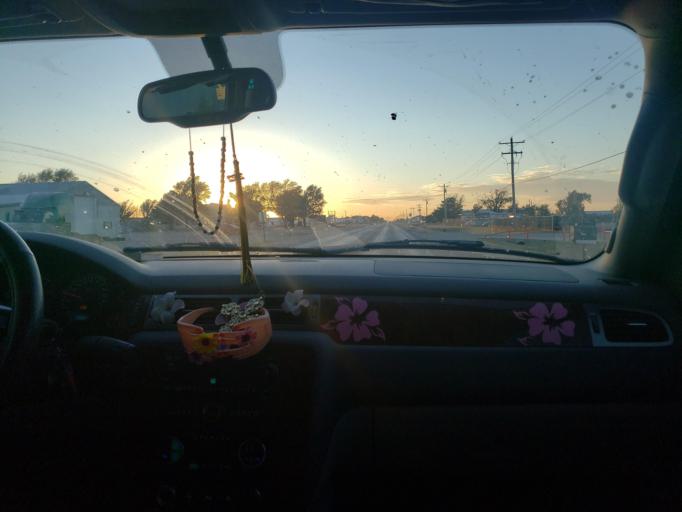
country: US
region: Kansas
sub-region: Finney County
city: Garden City
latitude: 37.9895
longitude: -100.9210
